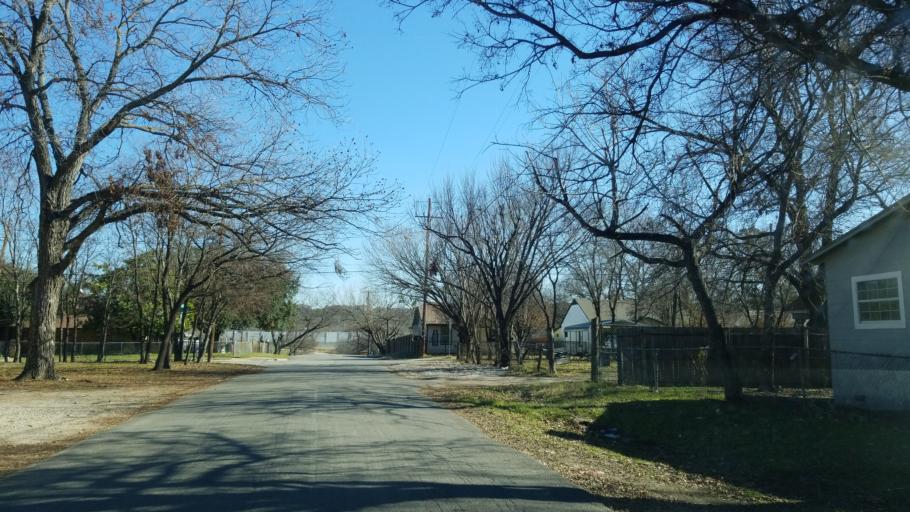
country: US
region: Texas
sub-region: Dallas County
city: Cockrell Hill
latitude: 32.7527
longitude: -96.9095
